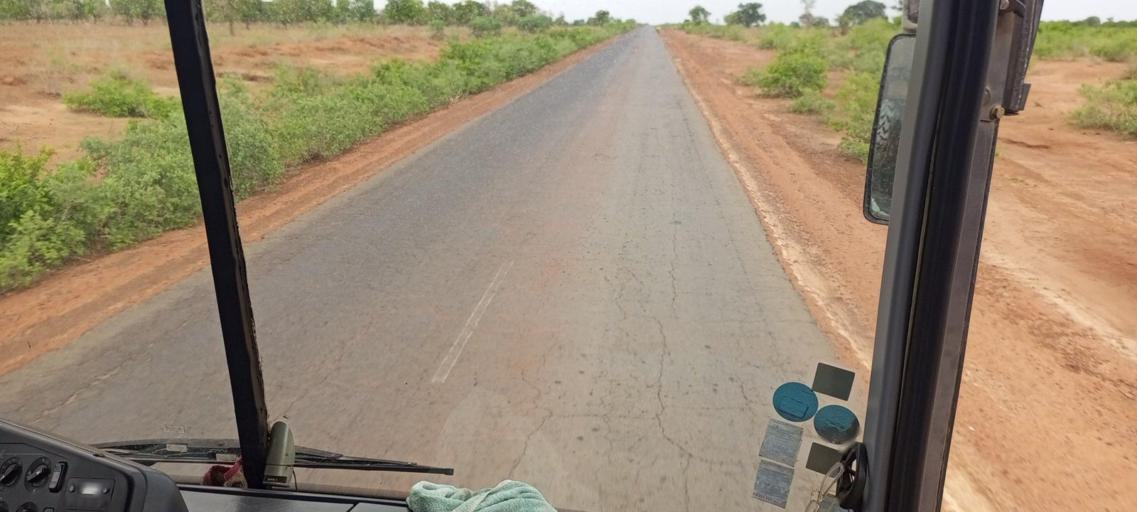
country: ML
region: Segou
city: Bla
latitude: 12.7176
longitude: -5.7248
